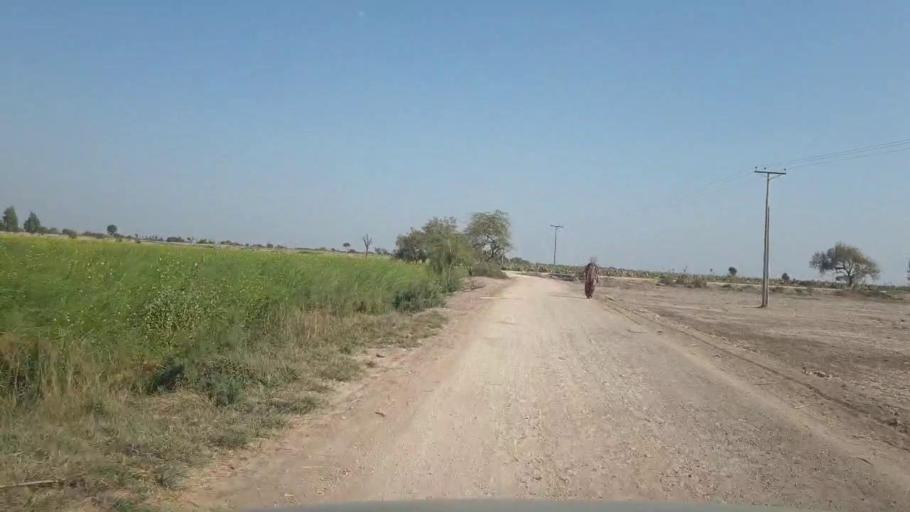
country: PK
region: Sindh
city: Chambar
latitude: 25.3245
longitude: 68.8667
